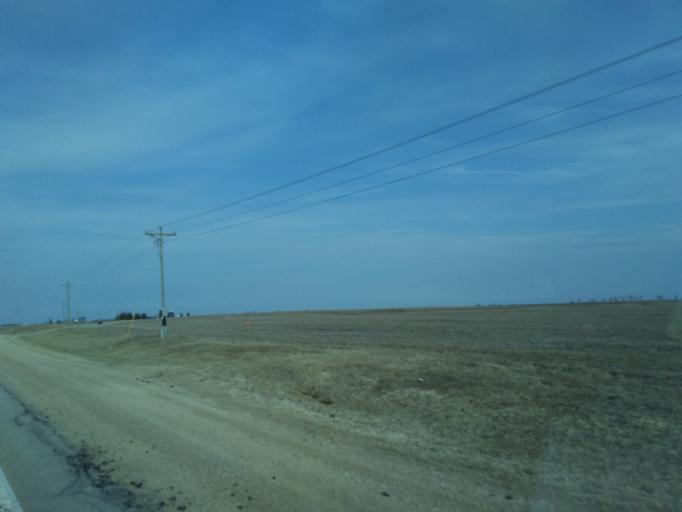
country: US
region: Wisconsin
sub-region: Grant County
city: Lancaster
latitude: 42.9629
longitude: -90.9109
